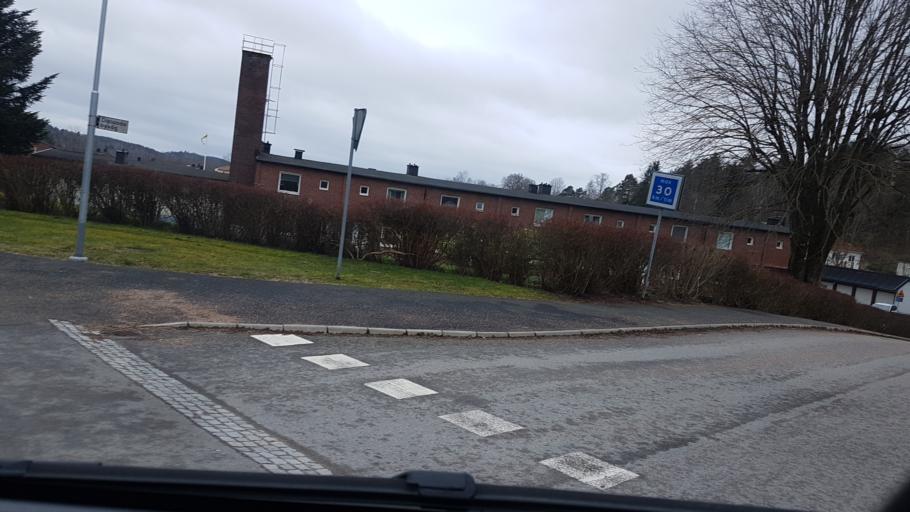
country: SE
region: Vaestra Goetaland
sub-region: Lerums Kommun
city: Stenkullen
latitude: 57.7907
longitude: 12.3085
